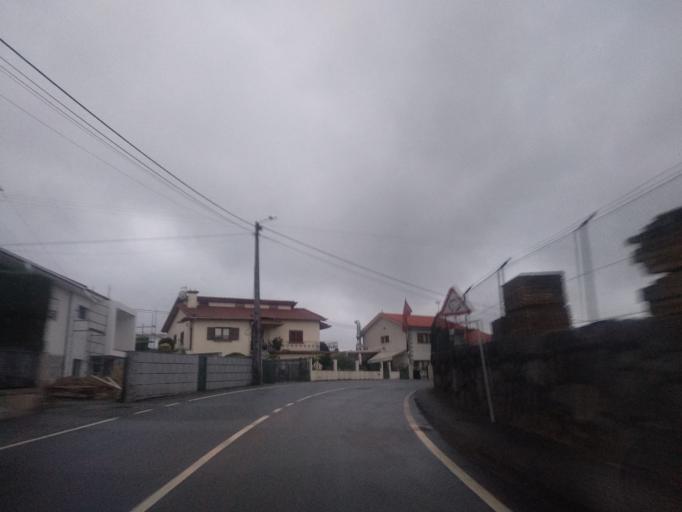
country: PT
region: Braga
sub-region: Guimaraes
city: Ponte
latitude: 41.4860
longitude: -8.3179
